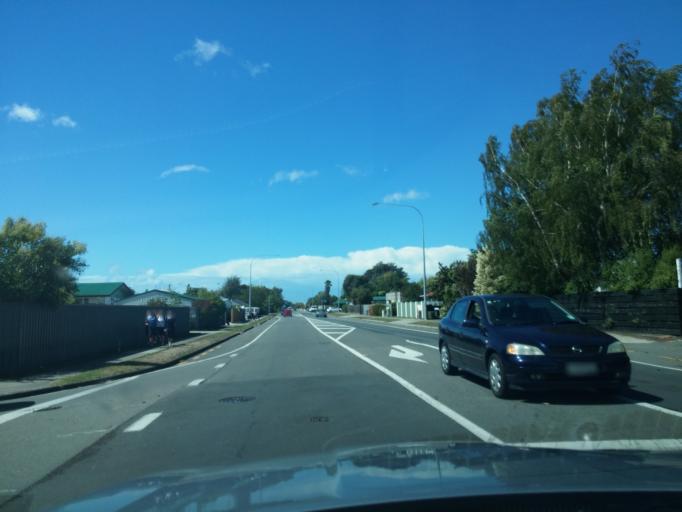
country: NZ
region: Marlborough
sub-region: Marlborough District
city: Blenheim
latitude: -41.5087
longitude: 173.9450
